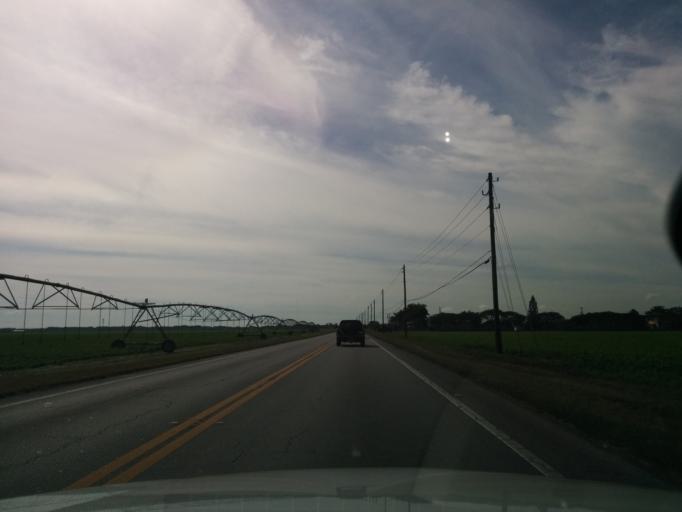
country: US
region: Florida
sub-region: Miami-Dade County
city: Country Walk
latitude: 25.6343
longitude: -80.4798
